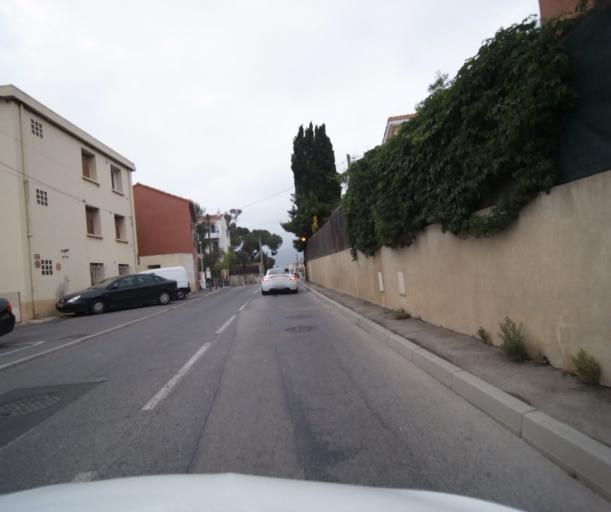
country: FR
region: Provence-Alpes-Cote d'Azur
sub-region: Departement du Var
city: La Seyne-sur-Mer
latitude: 43.0955
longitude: 5.8886
